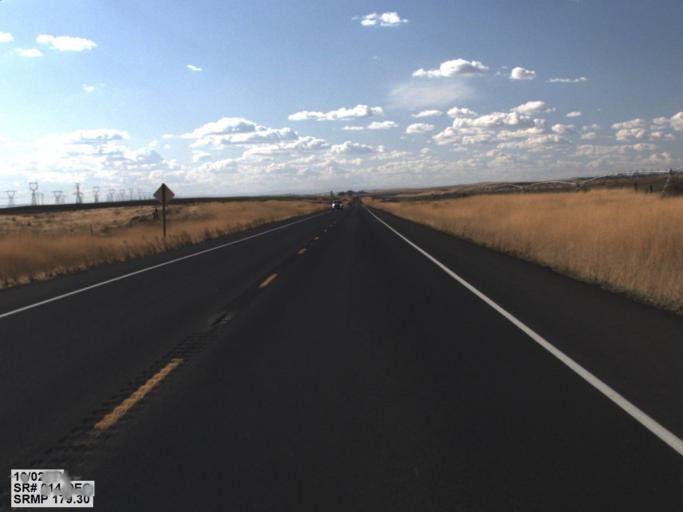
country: US
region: Oregon
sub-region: Umatilla County
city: Umatilla
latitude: 45.9459
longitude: -119.3649
